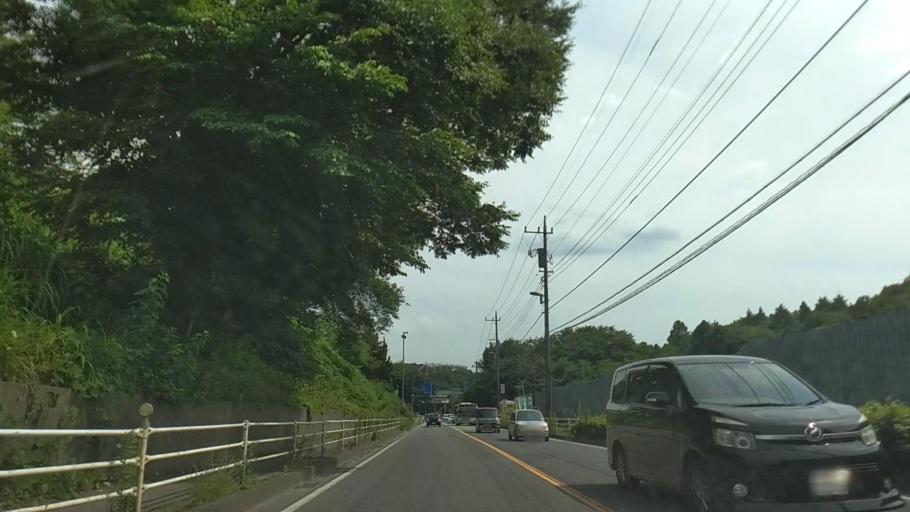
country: JP
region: Tokyo
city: Hachioji
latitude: 35.6180
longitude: 139.3410
